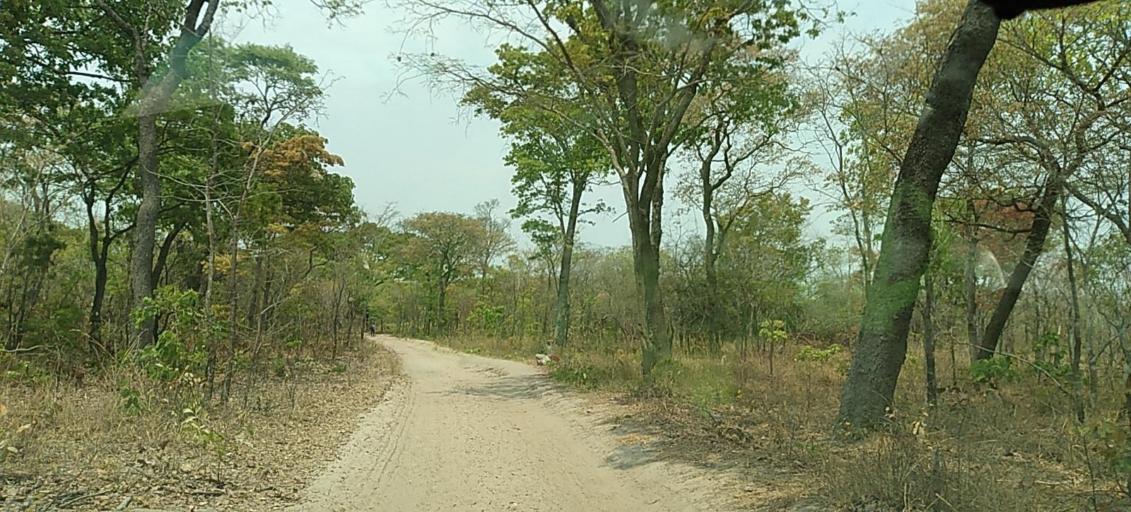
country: ZM
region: North-Western
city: Kabompo
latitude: -13.5446
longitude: 24.4506
